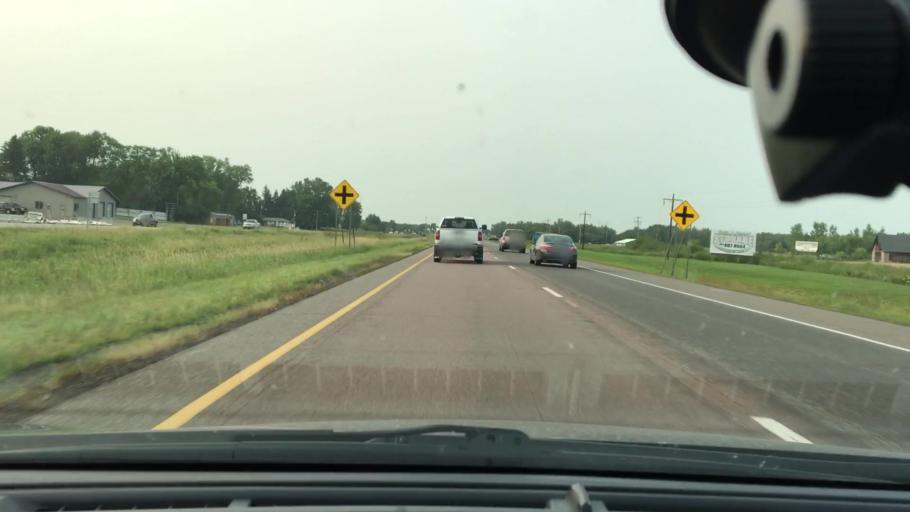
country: US
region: Minnesota
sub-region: Mille Lacs County
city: Milaca
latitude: 45.6957
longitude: -93.6412
